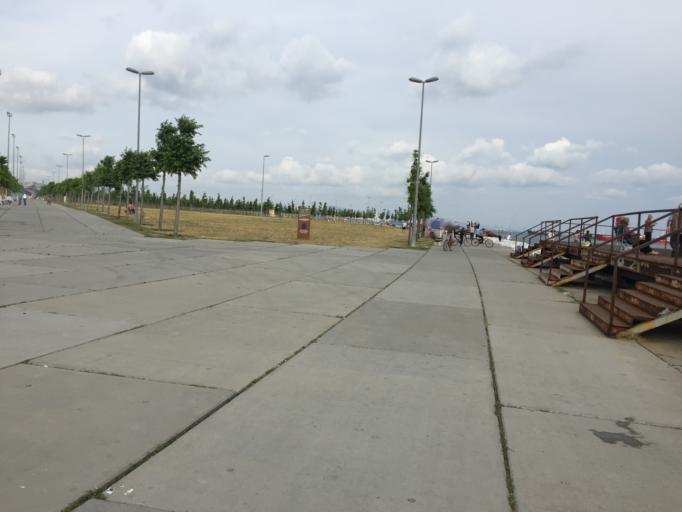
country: TR
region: Istanbul
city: Istanbul
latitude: 40.9969
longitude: 28.9425
